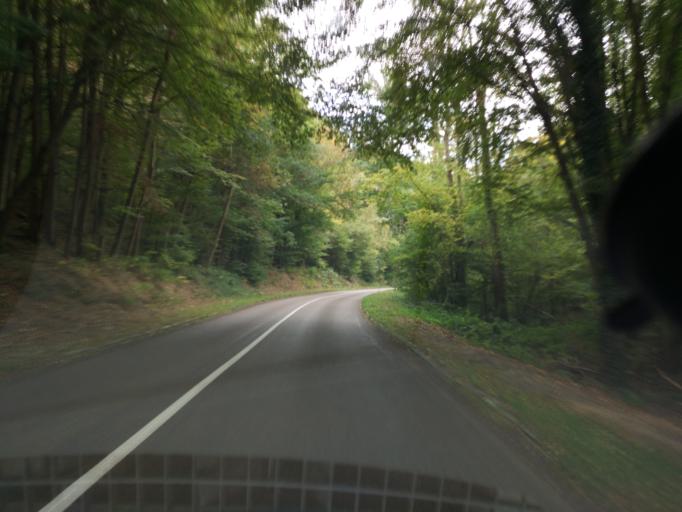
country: FR
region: Ile-de-France
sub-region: Departement de l'Essonne
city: Les Molieres
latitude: 48.6881
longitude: 2.0651
